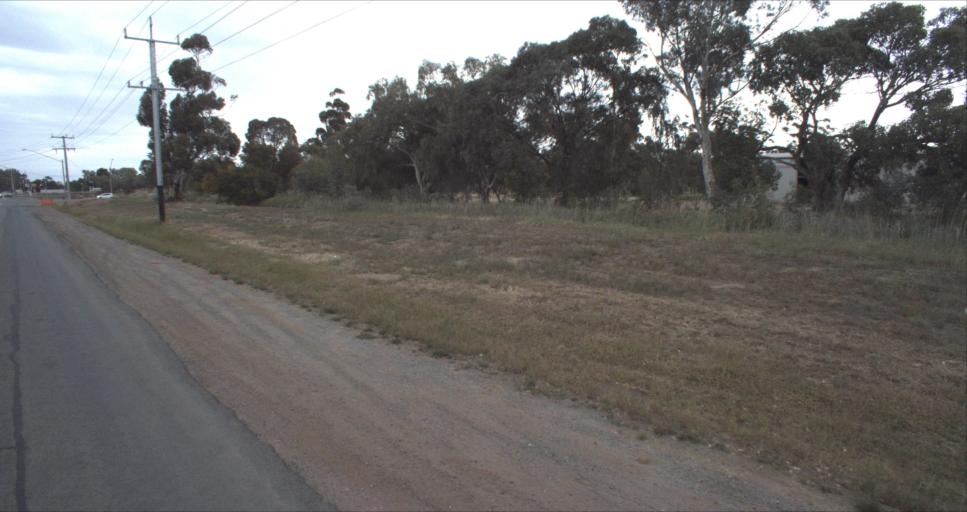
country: AU
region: New South Wales
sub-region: Leeton
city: Leeton
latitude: -34.5492
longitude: 146.3854
